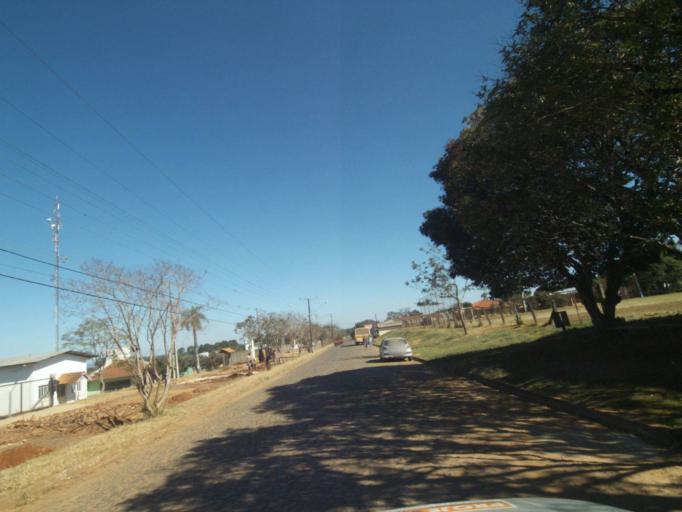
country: BR
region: Parana
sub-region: Reserva
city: Reserva
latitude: -24.6224
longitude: -50.6395
